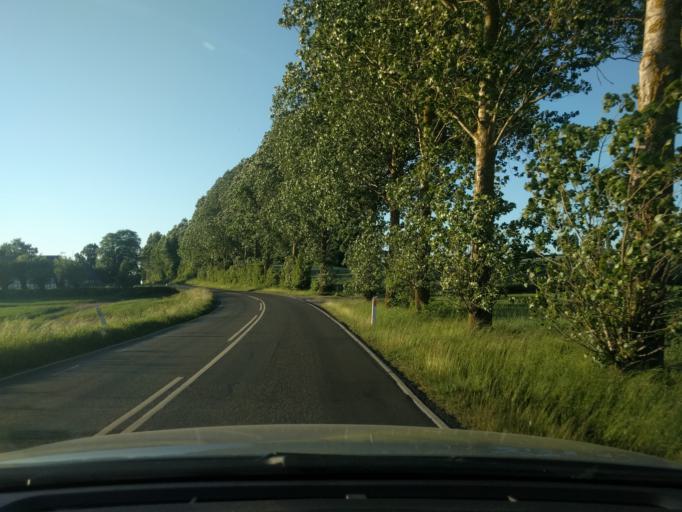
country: DK
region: South Denmark
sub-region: Kerteminde Kommune
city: Kerteminde
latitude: 55.5112
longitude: 10.6515
